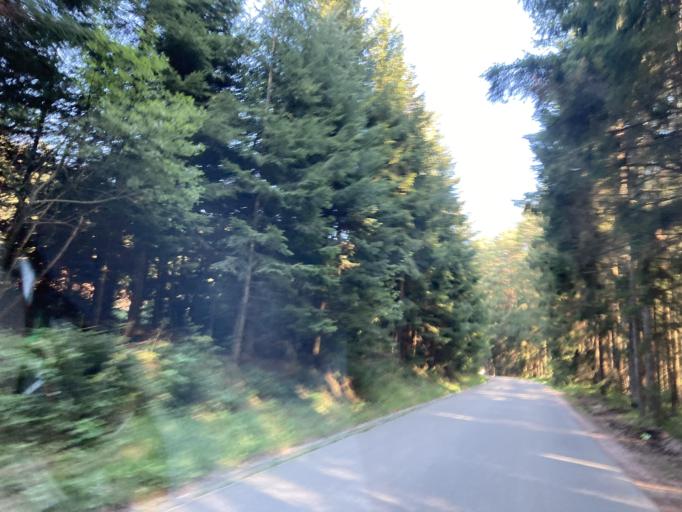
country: DE
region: Baden-Wuerttemberg
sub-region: Freiburg Region
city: Sankt Georgen im Schwarzwald
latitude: 48.1385
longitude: 8.2900
